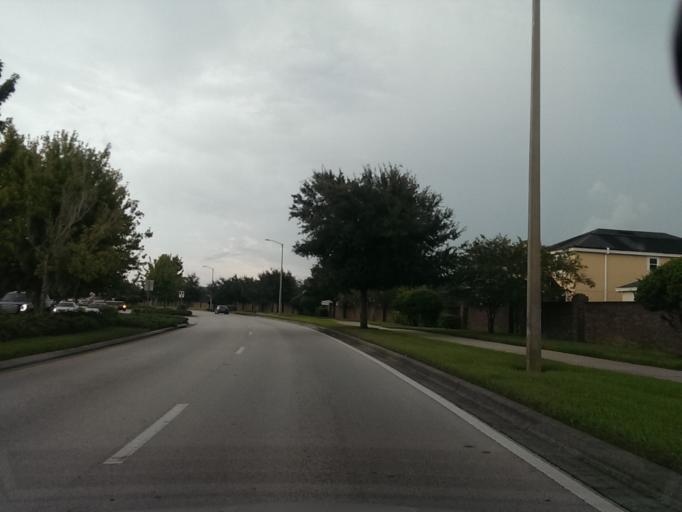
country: US
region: Florida
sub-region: Orange County
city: Winter Garden
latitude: 28.5309
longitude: -81.5821
